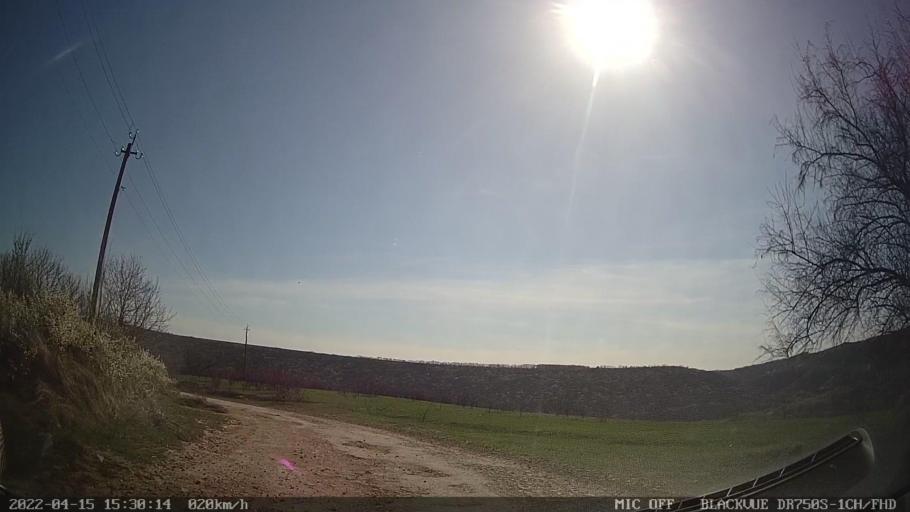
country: MD
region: Raionul Ocnita
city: Otaci
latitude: 48.3553
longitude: 27.9225
